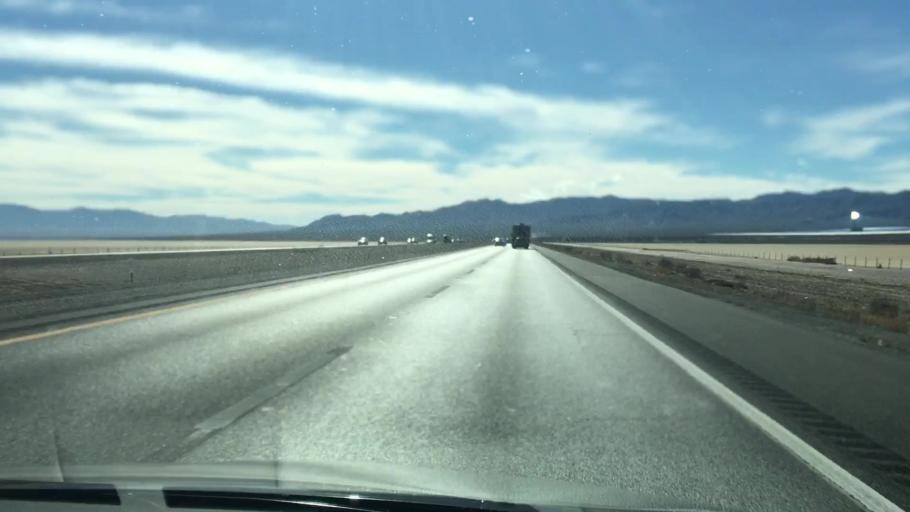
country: US
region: Nevada
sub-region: Clark County
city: Sandy Valley
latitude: 35.5894
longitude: -115.3993
